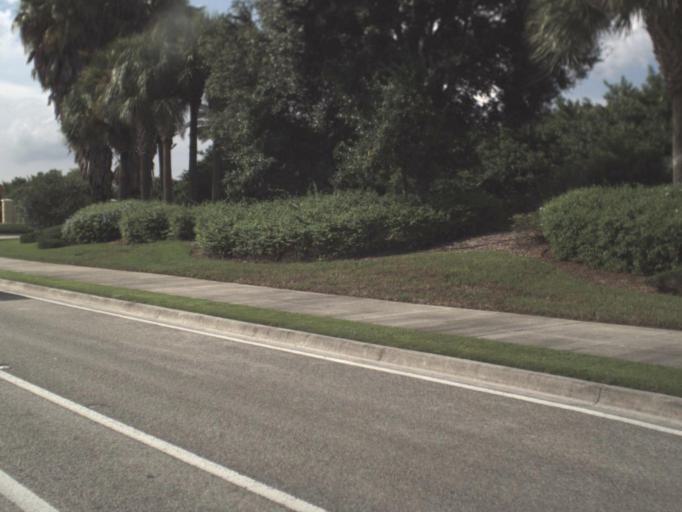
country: US
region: Florida
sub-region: Manatee County
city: Ellenton
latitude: 27.4866
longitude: -82.4599
